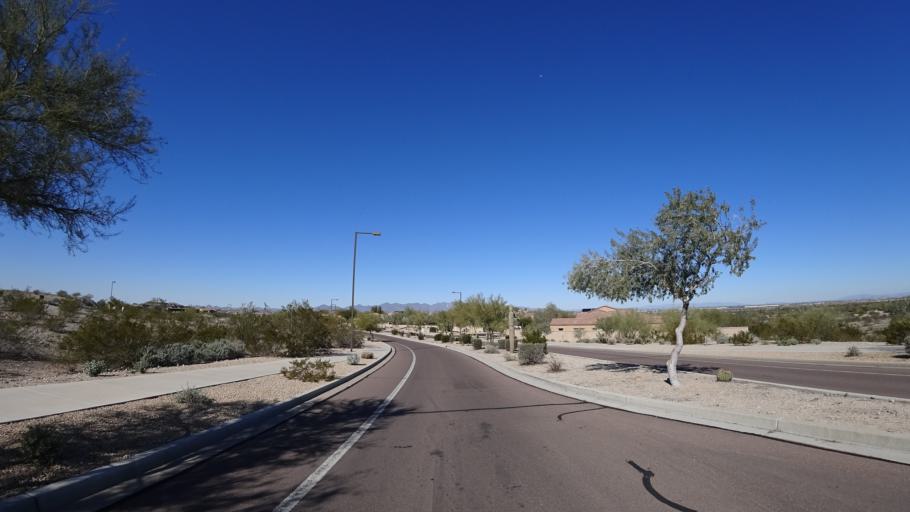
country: US
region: Arizona
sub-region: Maricopa County
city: Goodyear
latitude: 33.3608
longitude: -112.4320
